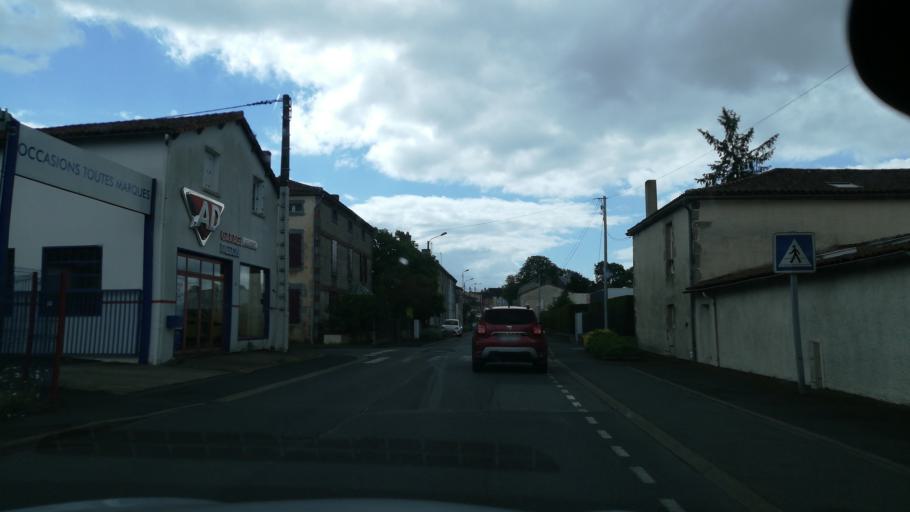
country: FR
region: Poitou-Charentes
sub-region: Departement des Deux-Sevres
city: Moncoutant
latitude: 46.7269
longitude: -0.5909
